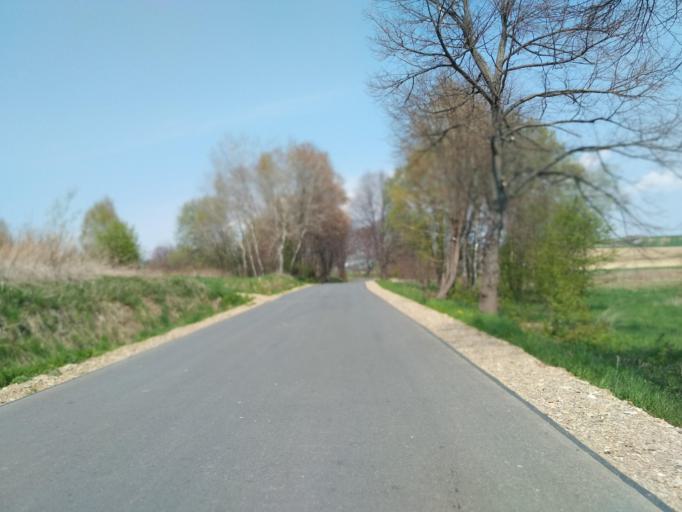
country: PL
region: Subcarpathian Voivodeship
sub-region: Powiat krosnienski
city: Chorkowka
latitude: 49.6383
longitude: 21.6865
